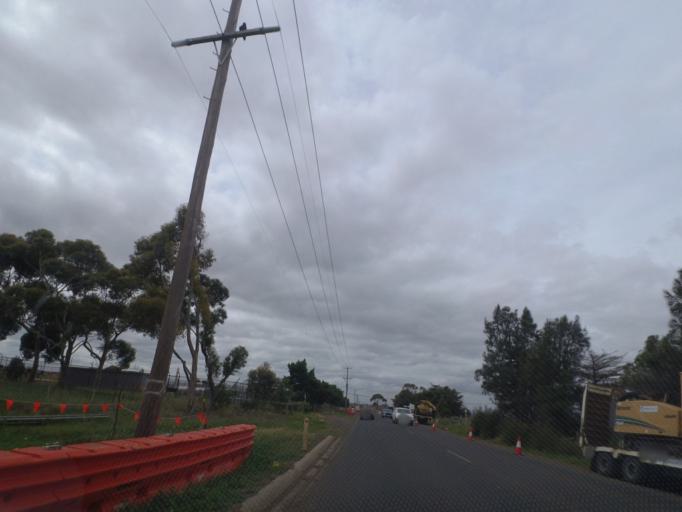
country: AU
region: Victoria
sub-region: Melton
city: Caroline Springs
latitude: -37.7188
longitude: 144.7111
